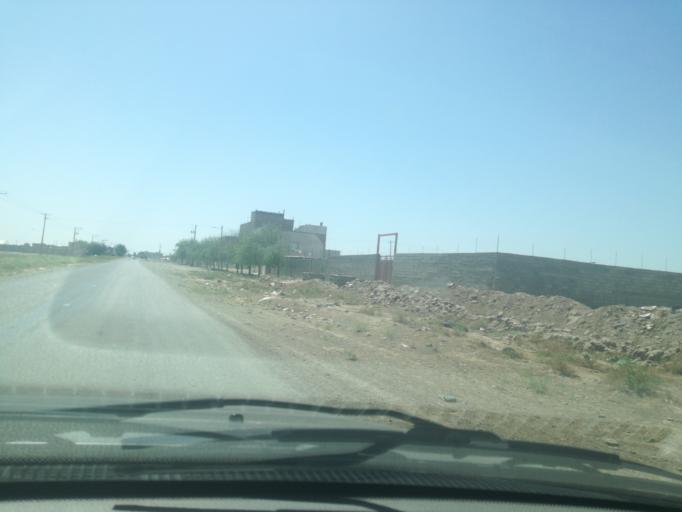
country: IR
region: Razavi Khorasan
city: Sarakhs
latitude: 36.5661
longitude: 61.1419
